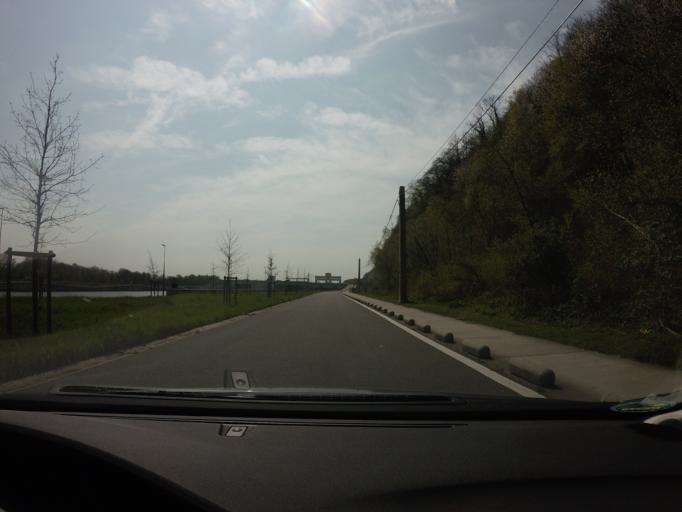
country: NL
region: Limburg
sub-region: Eijsden-Margraten
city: Eijsden
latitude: 50.8000
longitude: 5.6897
